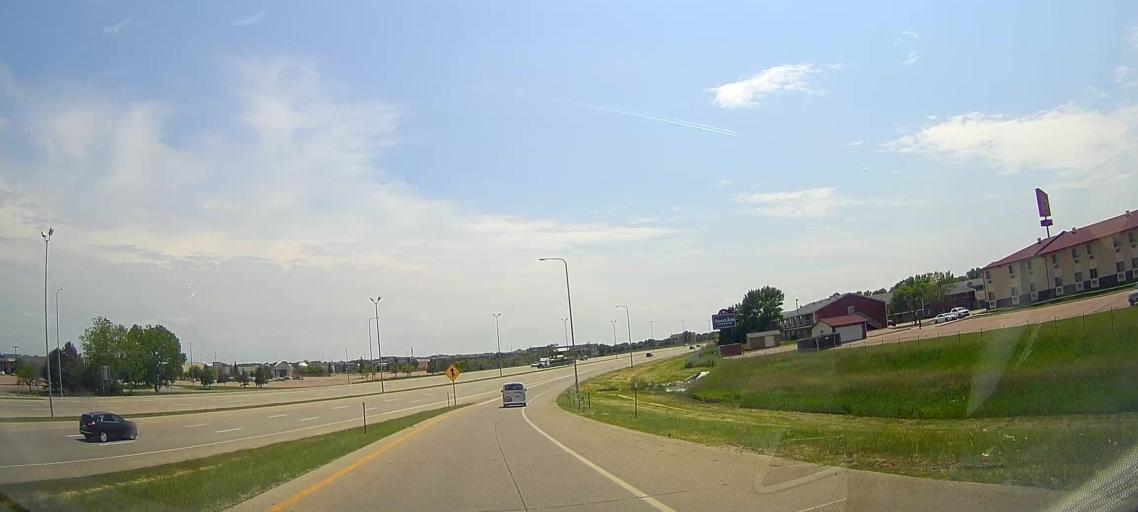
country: US
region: South Dakota
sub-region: Lincoln County
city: Tea
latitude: 43.5135
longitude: -96.7812
